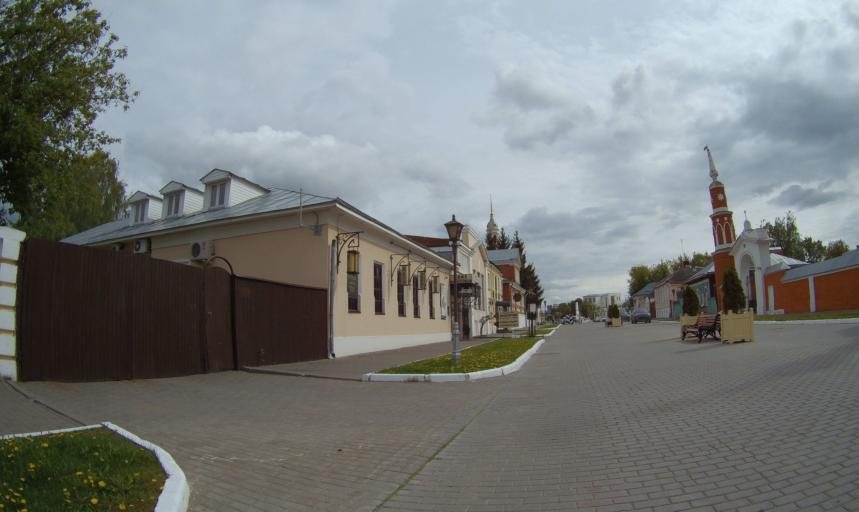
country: RU
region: Moskovskaya
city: Kolomna
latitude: 55.1045
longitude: 38.7547
